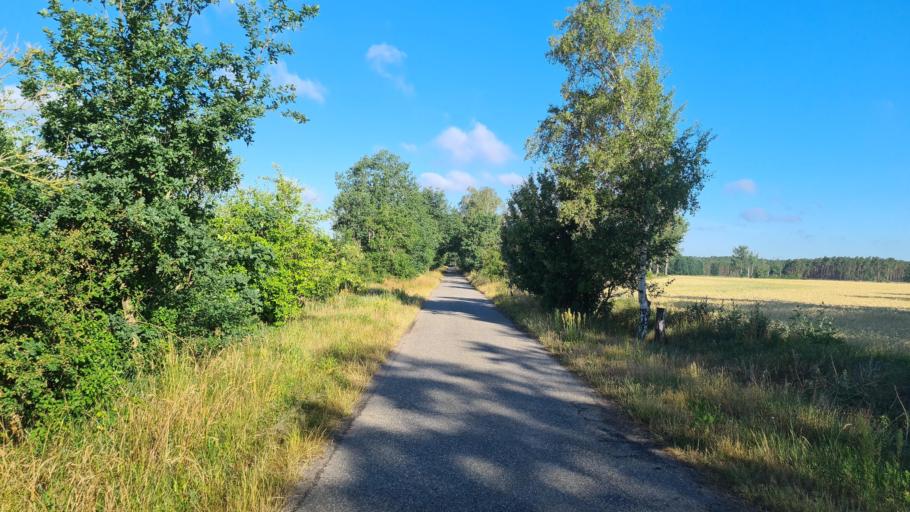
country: DE
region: Saxony
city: Beilrode
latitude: 51.6413
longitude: 13.1021
